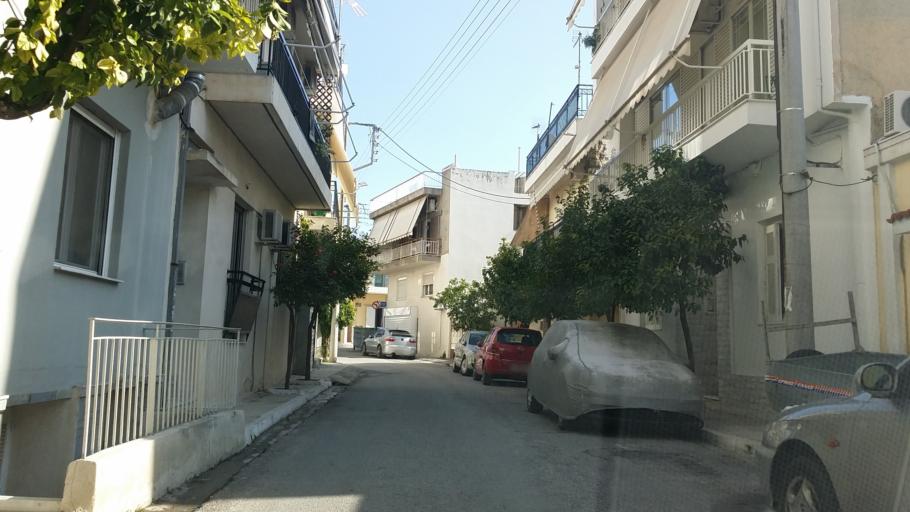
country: GR
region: Attica
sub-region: Nomarchia Athinas
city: Ilion
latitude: 38.0216
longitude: 23.7046
